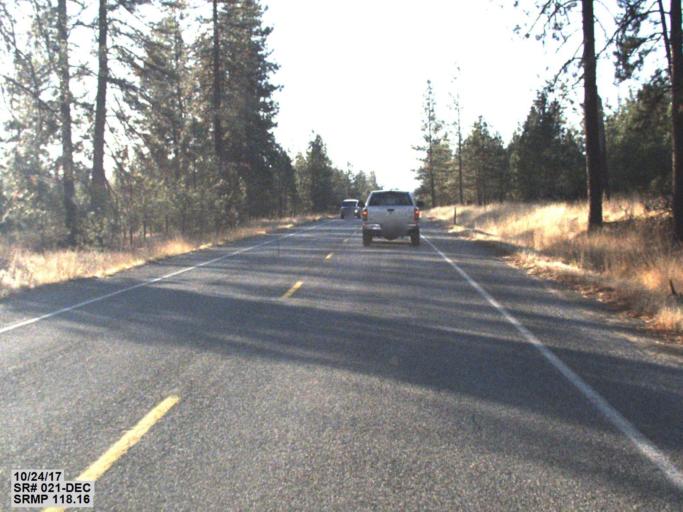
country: US
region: Washington
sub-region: Okanogan County
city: Coulee Dam
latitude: 48.0969
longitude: -118.6937
